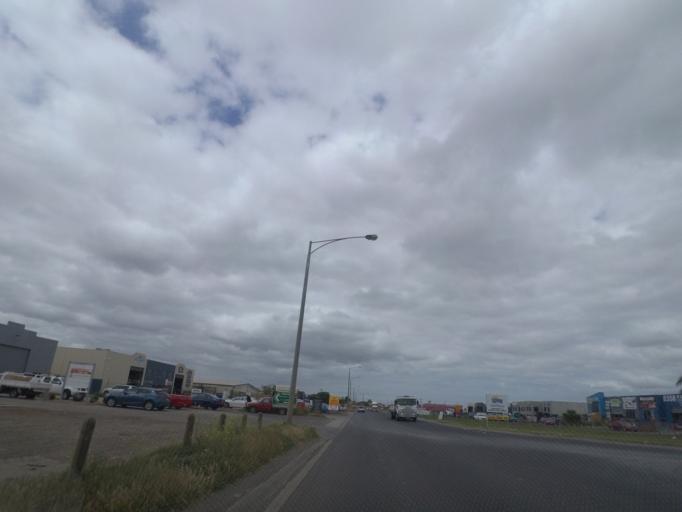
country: AU
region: Victoria
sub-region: Brimbank
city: Deer Park
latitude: -37.7670
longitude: 144.7532
